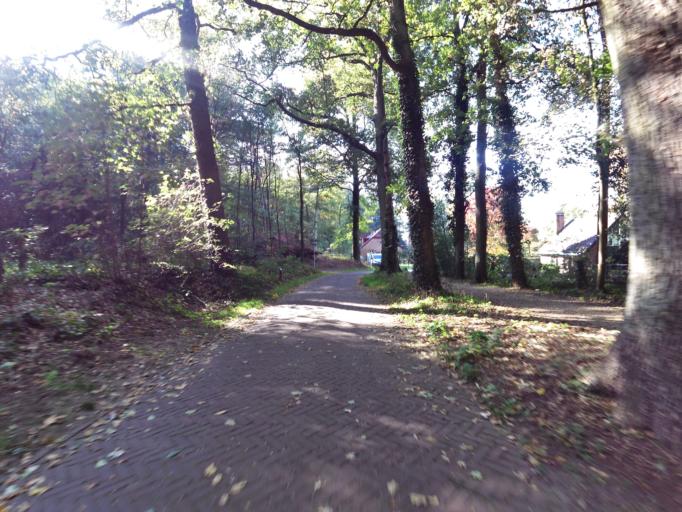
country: NL
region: Gelderland
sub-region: Gemeente Rheden
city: Velp
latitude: 52.0072
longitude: 5.9863
